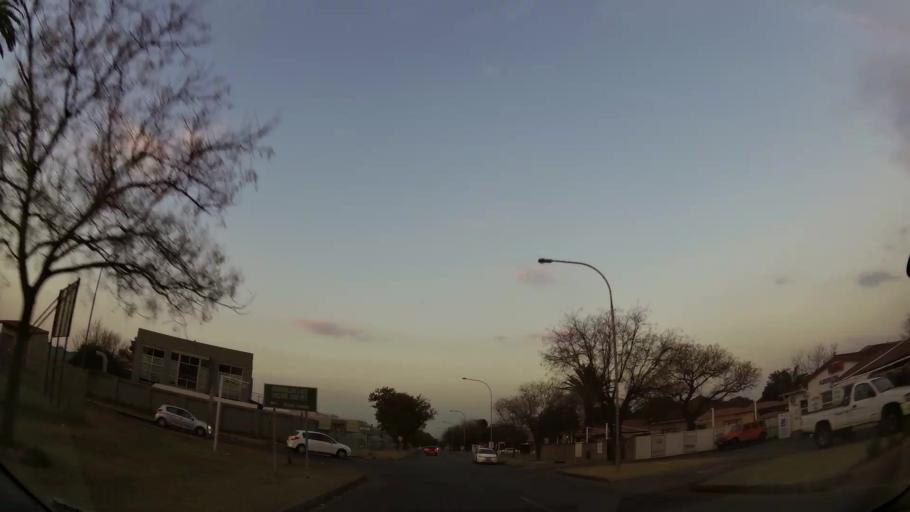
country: ZA
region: Gauteng
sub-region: Ekurhuleni Metropolitan Municipality
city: Benoni
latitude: -26.1639
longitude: 28.3204
